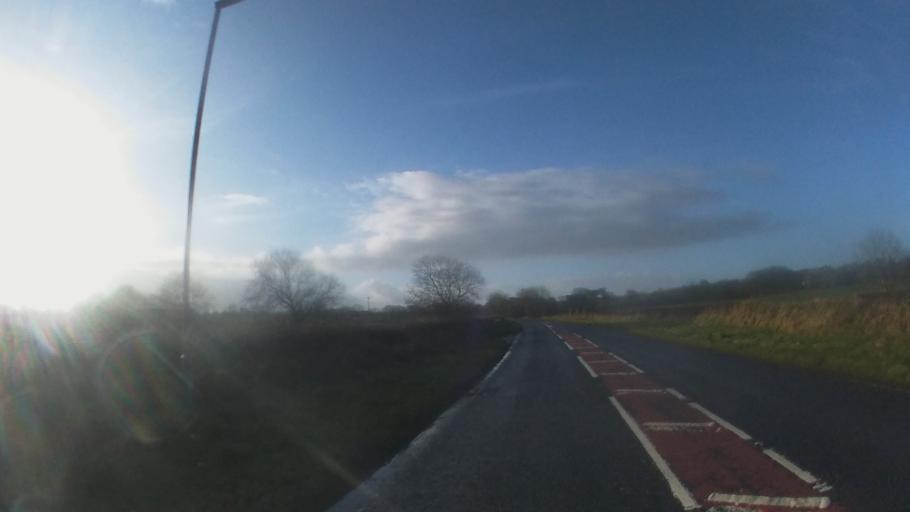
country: GB
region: Northern Ireland
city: Bushmills
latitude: 55.2311
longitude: -6.5180
